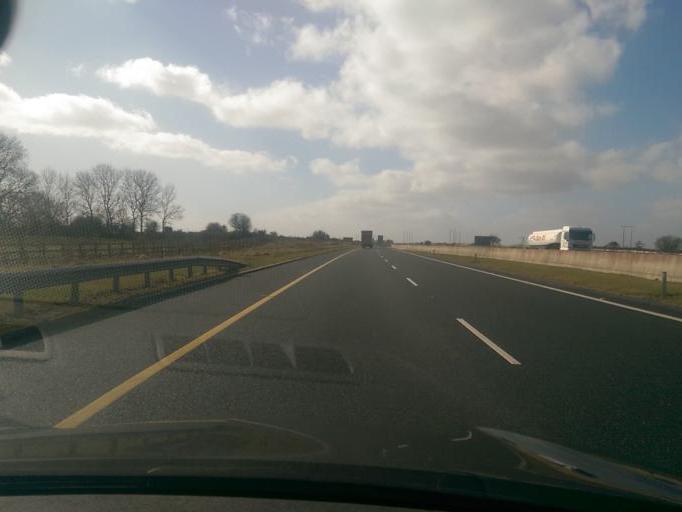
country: IE
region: Connaught
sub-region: County Galway
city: Oranmore
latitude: 53.2969
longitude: -8.9004
